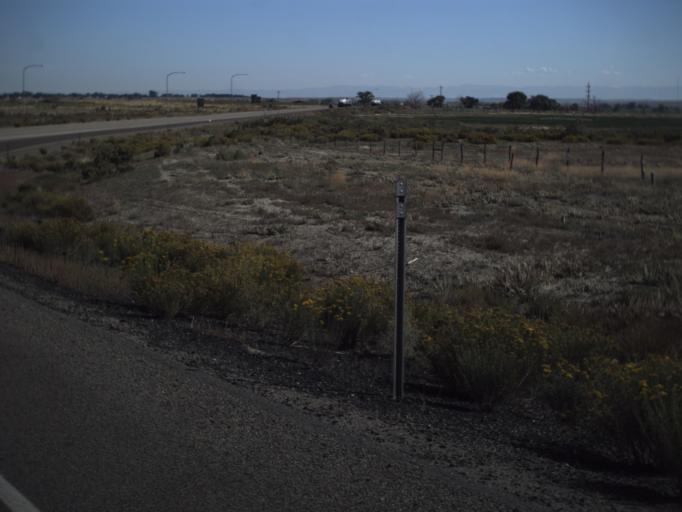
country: US
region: Utah
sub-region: Emery County
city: Castle Dale
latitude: 39.1763
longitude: -111.0458
